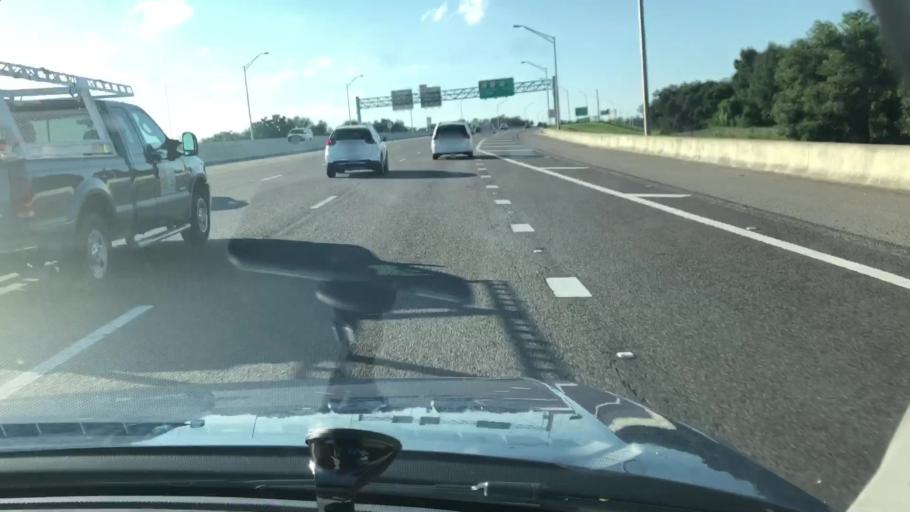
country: US
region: Florida
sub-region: Orange County
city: South Apopka
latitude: 28.6467
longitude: -81.5139
